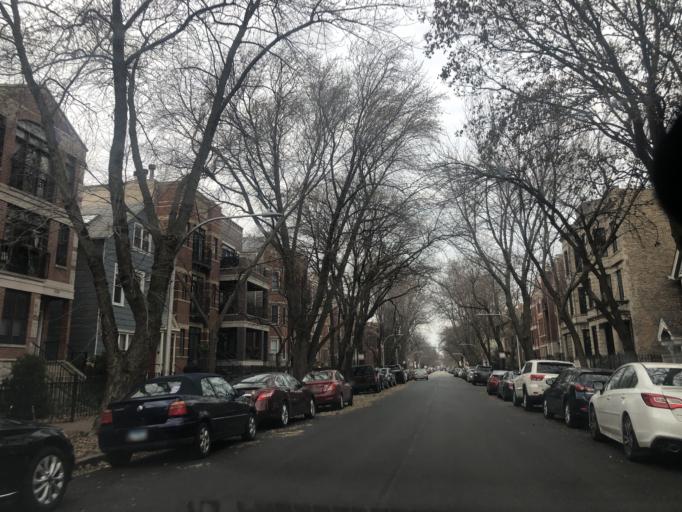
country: US
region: Illinois
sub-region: Cook County
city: Chicago
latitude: 41.9403
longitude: -87.6565
